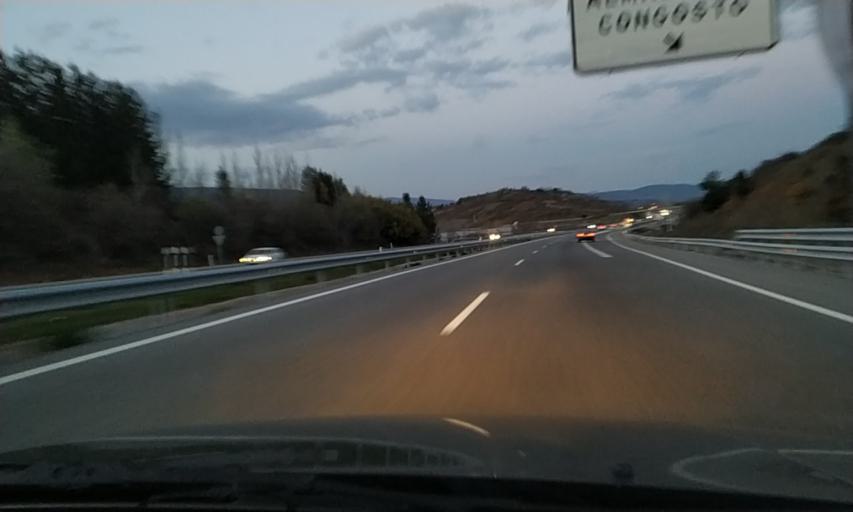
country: ES
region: Castille and Leon
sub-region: Provincia de Leon
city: Congosto
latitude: 42.5897
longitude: -6.5228
